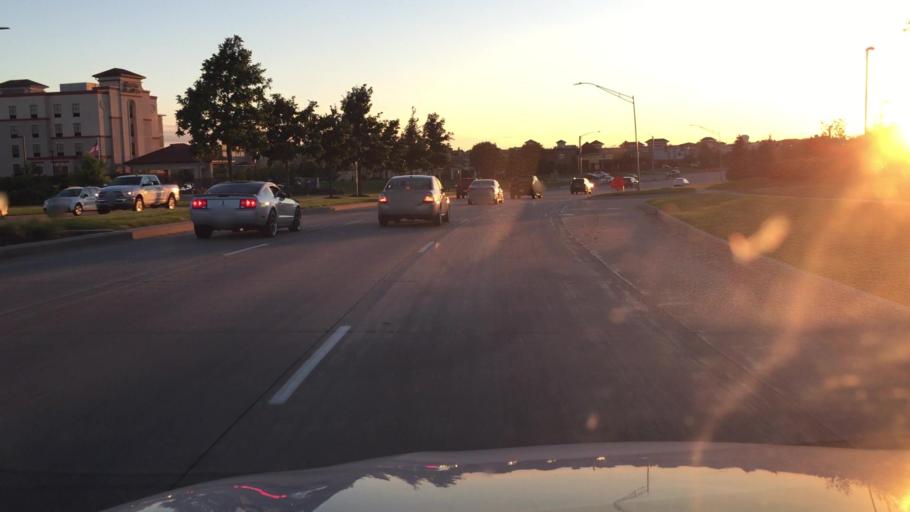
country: US
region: Iowa
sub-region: Polk County
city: Clive
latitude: 41.5592
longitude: -93.7918
